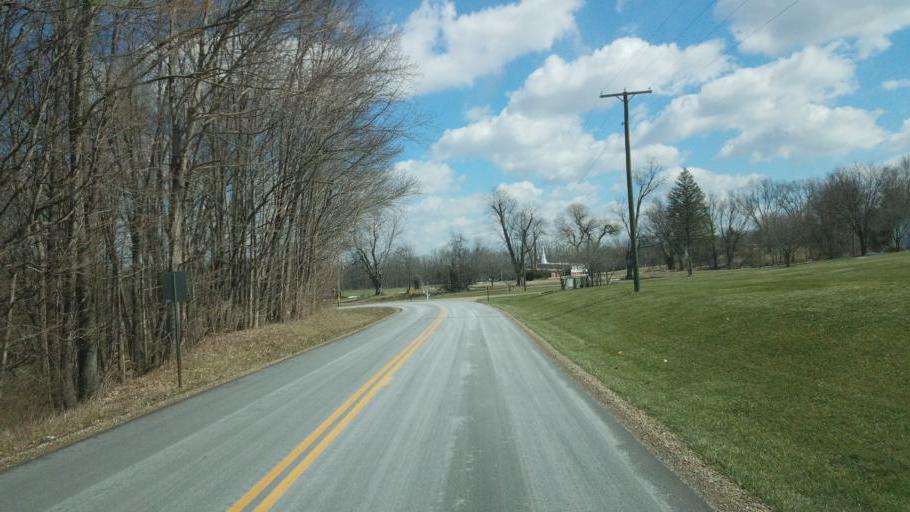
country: US
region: Ohio
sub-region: Knox County
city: Mount Vernon
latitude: 40.3476
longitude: -82.5527
